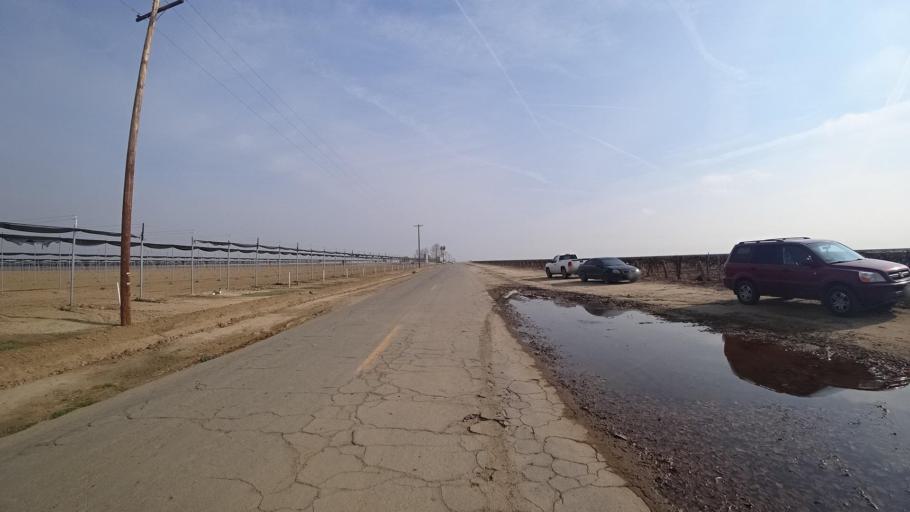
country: US
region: California
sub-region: Kern County
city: Lebec
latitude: 35.0309
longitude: -118.9124
